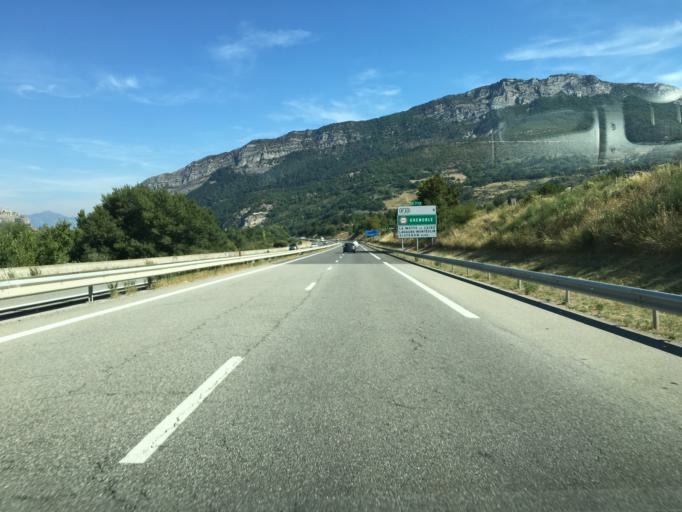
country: FR
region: Provence-Alpes-Cote d'Azur
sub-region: Departement des Alpes-de-Haute-Provence
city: Sisteron
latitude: 44.1767
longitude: 5.9544
